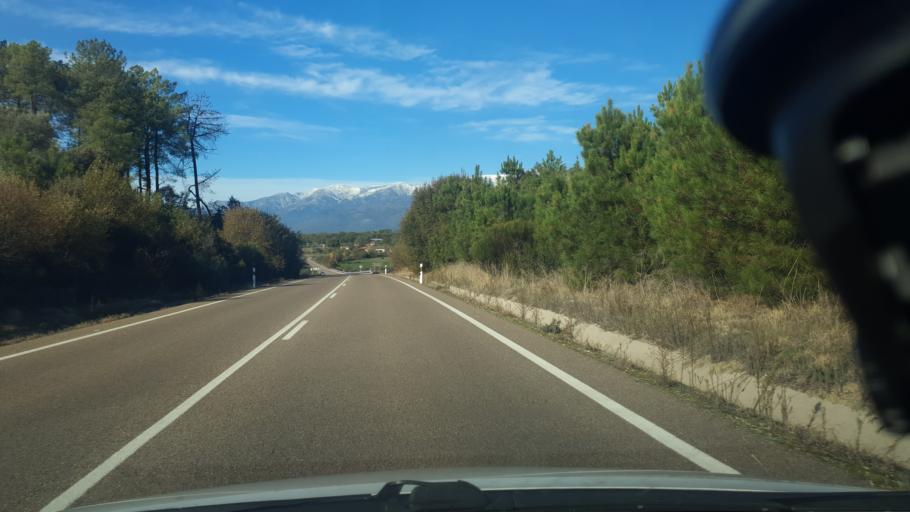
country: ES
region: Castille and Leon
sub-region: Provincia de Avila
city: Candeleda
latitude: 40.1361
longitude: -5.2362
